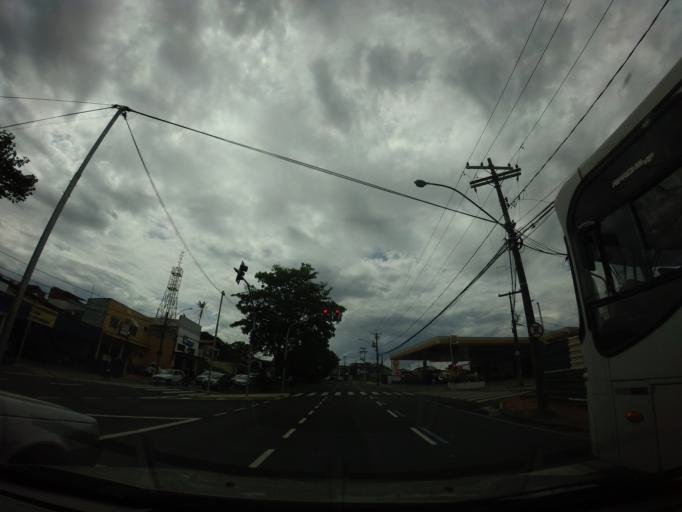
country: BR
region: Sao Paulo
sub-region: Piracicaba
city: Piracicaba
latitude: -22.7331
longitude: -47.6340
